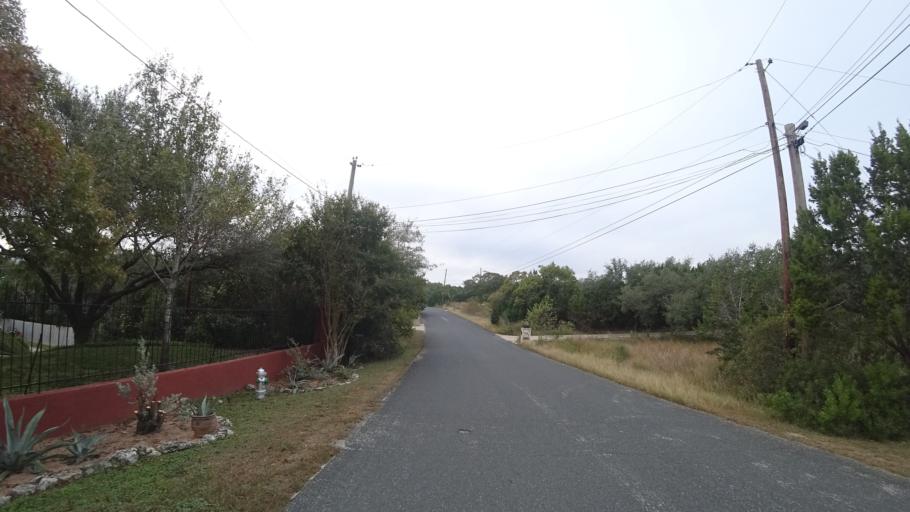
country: US
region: Texas
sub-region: Travis County
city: Hudson Bend
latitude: 30.3873
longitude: -97.9174
